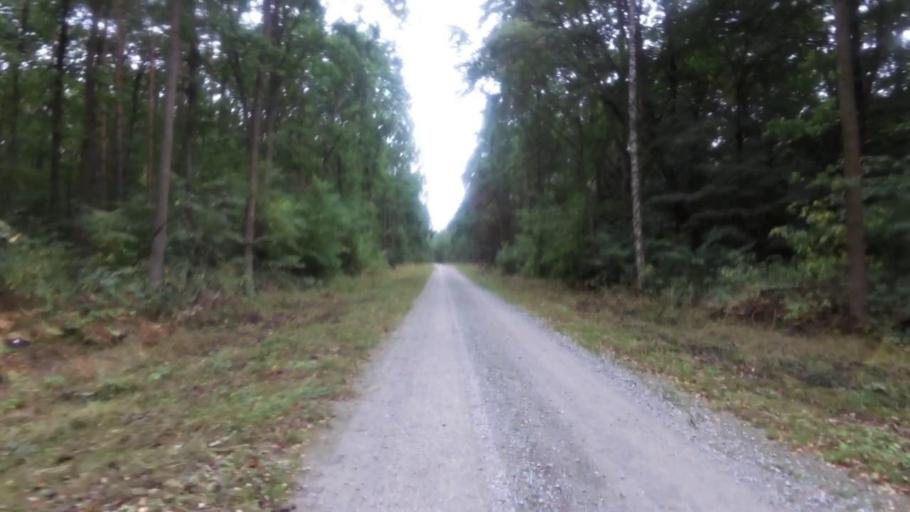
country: PL
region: Lubusz
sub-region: Powiat gorzowski
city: Kostrzyn nad Odra
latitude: 52.6358
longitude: 14.6467
